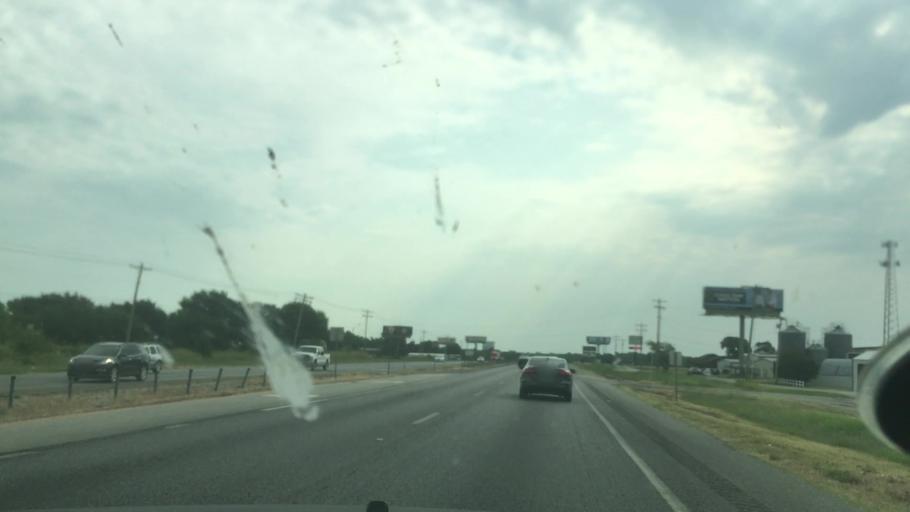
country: US
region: Oklahoma
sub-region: Bryan County
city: Calera
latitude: 33.9148
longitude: -96.4534
